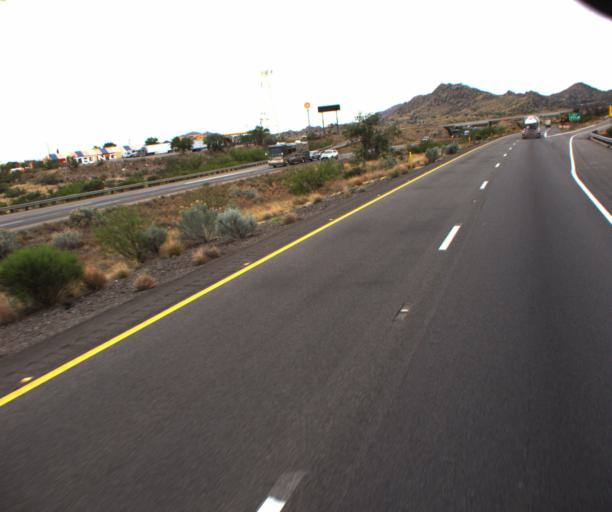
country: US
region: Arizona
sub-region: Cochise County
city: Saint David
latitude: 32.0833
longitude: -110.0489
